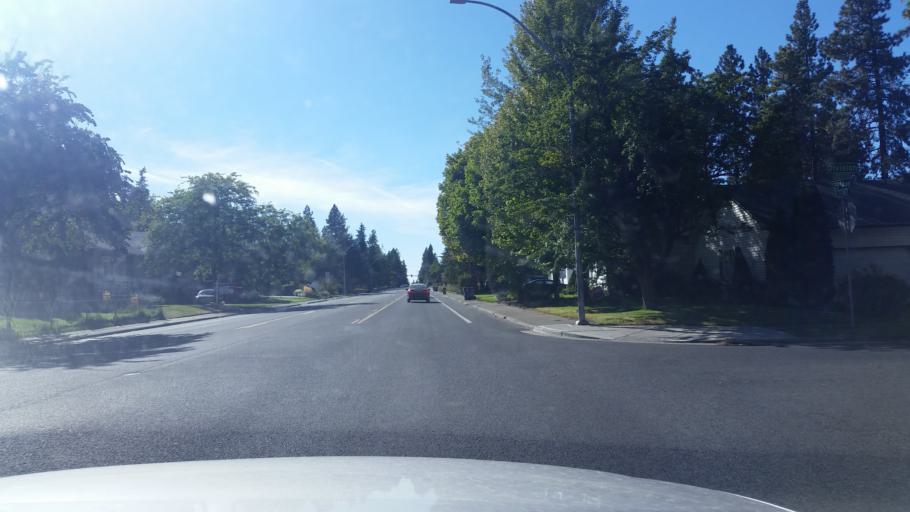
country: US
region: Washington
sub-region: Spokane County
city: Spokane
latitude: 47.6282
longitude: -117.4112
